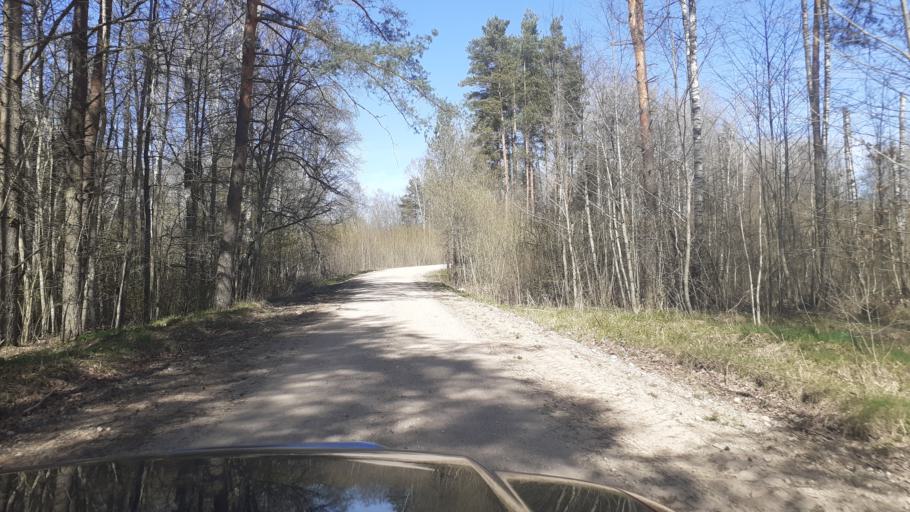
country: LV
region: Kuldigas Rajons
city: Kuldiga
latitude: 56.8459
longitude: 21.9780
